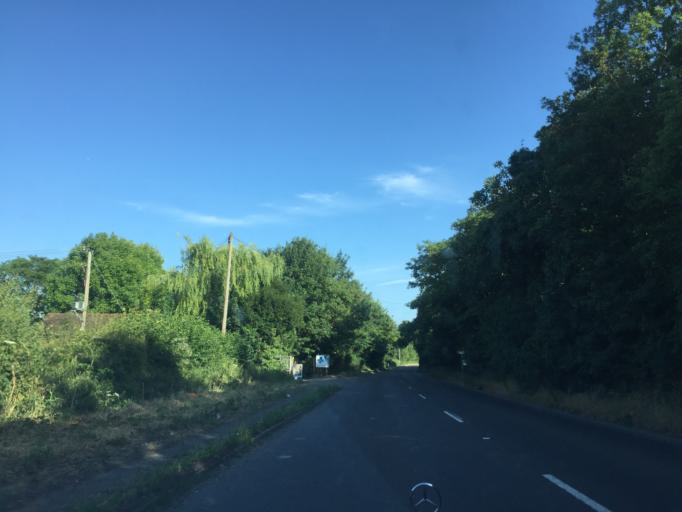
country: GB
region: England
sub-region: Oxfordshire
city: Chinnor
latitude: 51.6841
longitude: -0.9636
